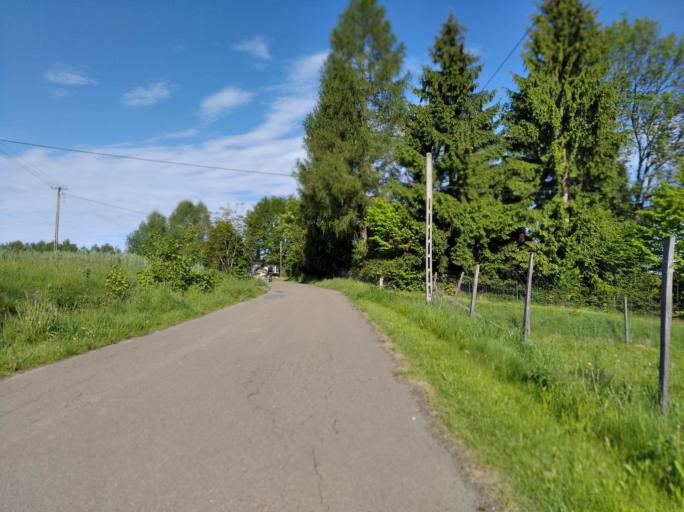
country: PL
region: Subcarpathian Voivodeship
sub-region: Powiat strzyzowski
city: Frysztak
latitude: 49.8442
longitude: 21.5579
